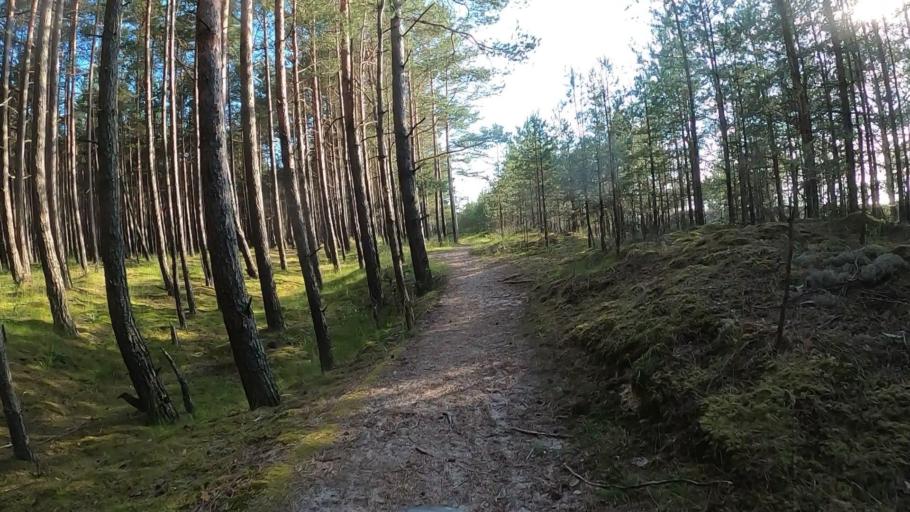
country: LV
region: Carnikava
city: Carnikava
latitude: 57.1210
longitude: 24.2058
